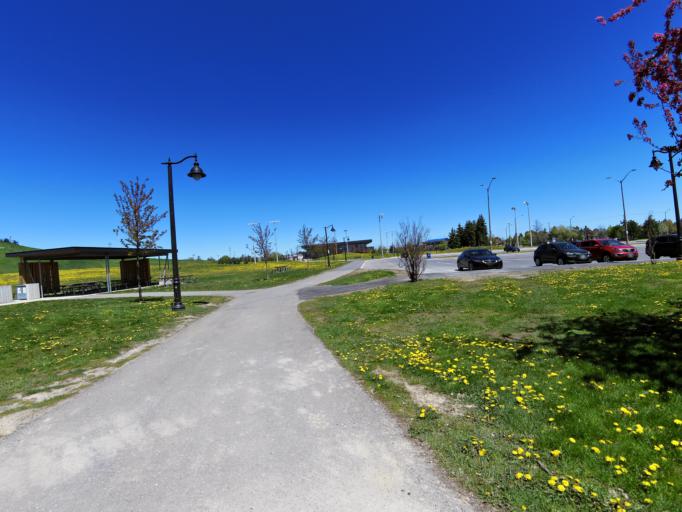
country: CA
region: Ontario
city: Brampton
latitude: 43.7254
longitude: -79.7233
